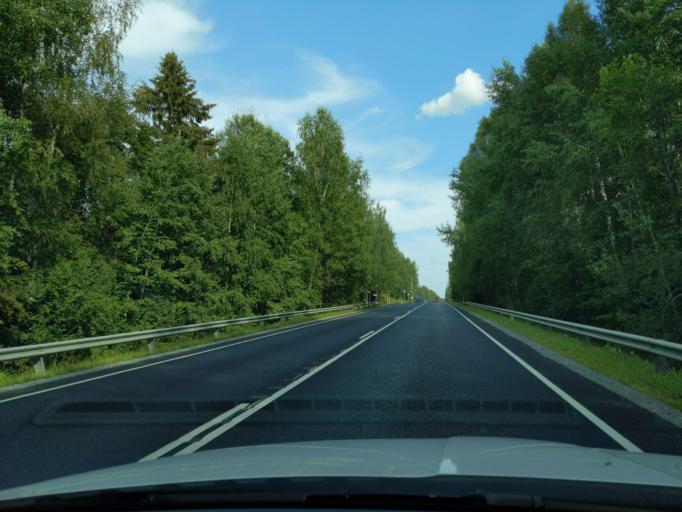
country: FI
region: Haeme
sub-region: Haemeenlinna
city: Tuulos
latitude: 61.1599
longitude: 24.6818
